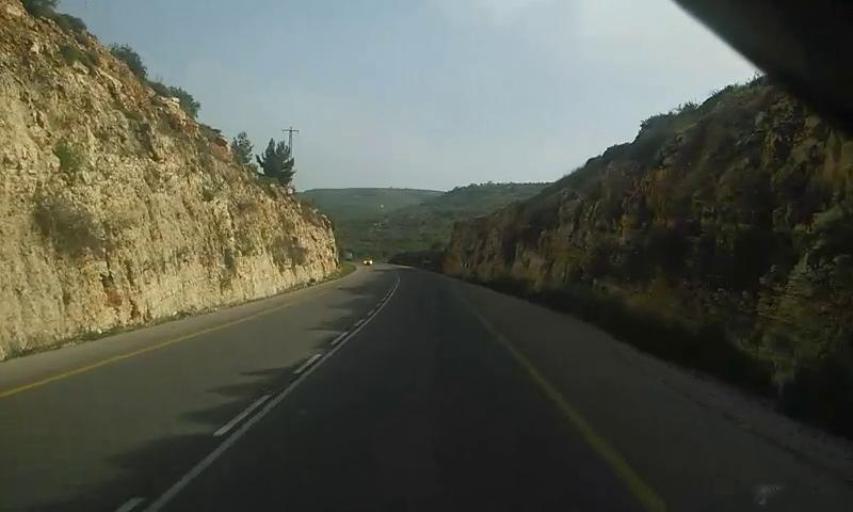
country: PS
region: West Bank
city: Jit
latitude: 32.2259
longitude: 35.1731
